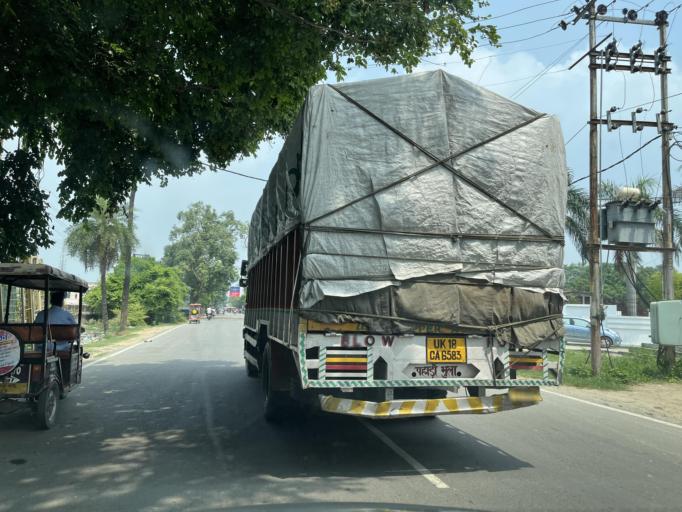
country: IN
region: Uttar Pradesh
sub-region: Bijnor
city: Najibabad
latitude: 29.5958
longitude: 78.3393
